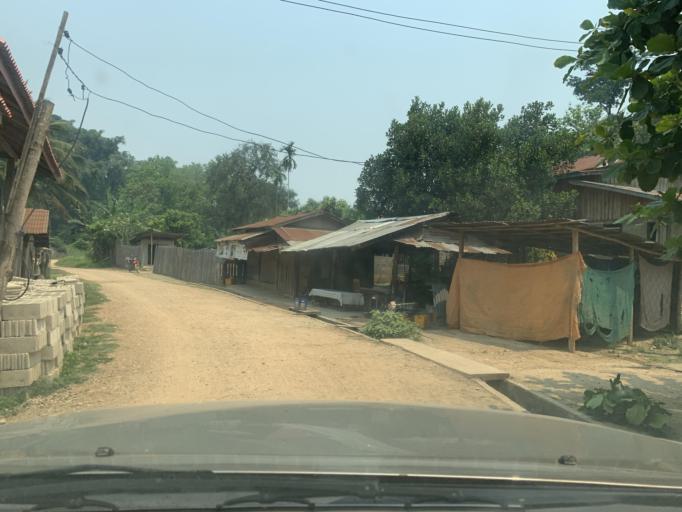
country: LA
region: Louangphabang
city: Xiang Ngeun
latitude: 19.8210
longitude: 102.2102
